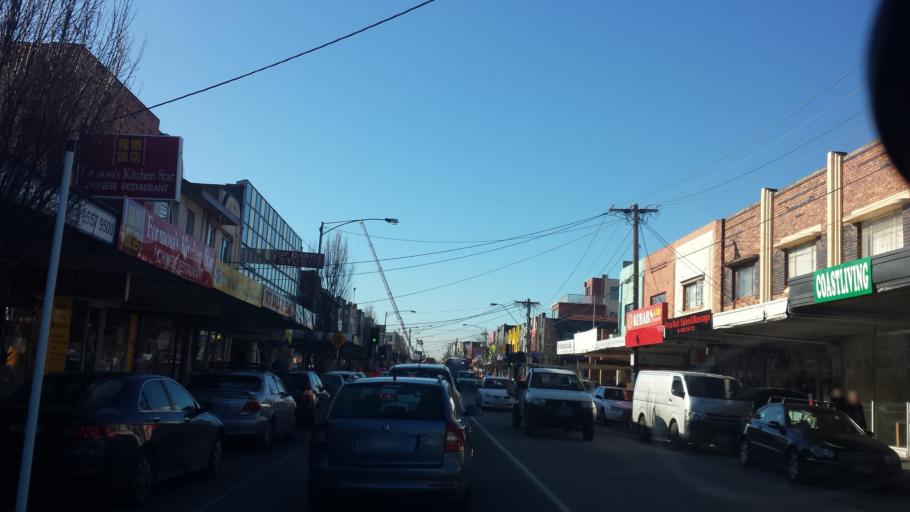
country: AU
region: Victoria
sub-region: Glen Eira
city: Bentleigh
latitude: -37.9178
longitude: 145.0345
